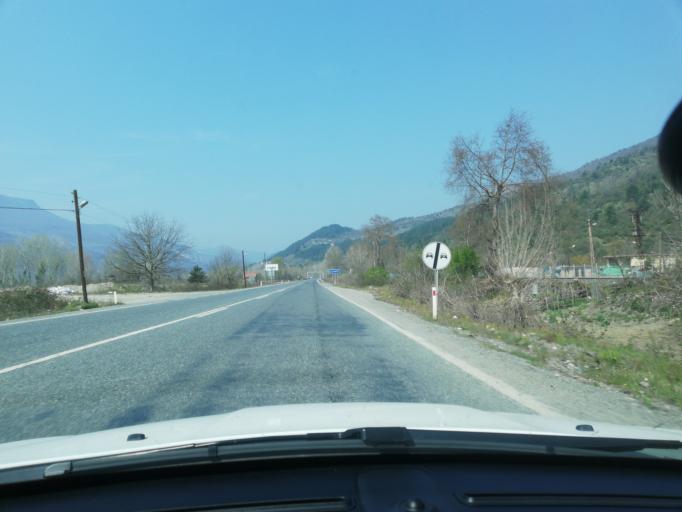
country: TR
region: Karabuk
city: Yenice
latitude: 41.2170
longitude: 32.3018
